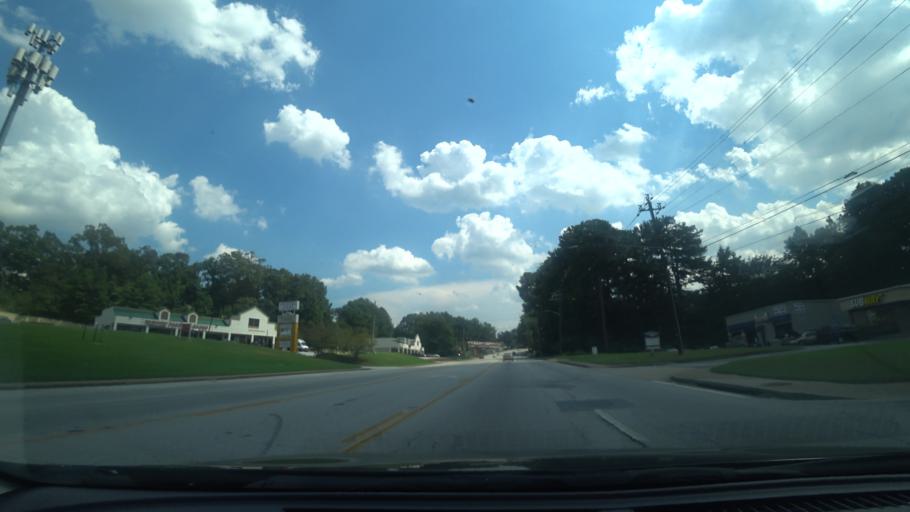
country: US
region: Georgia
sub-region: DeKalb County
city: Clarkston
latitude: 33.8237
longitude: -84.2330
